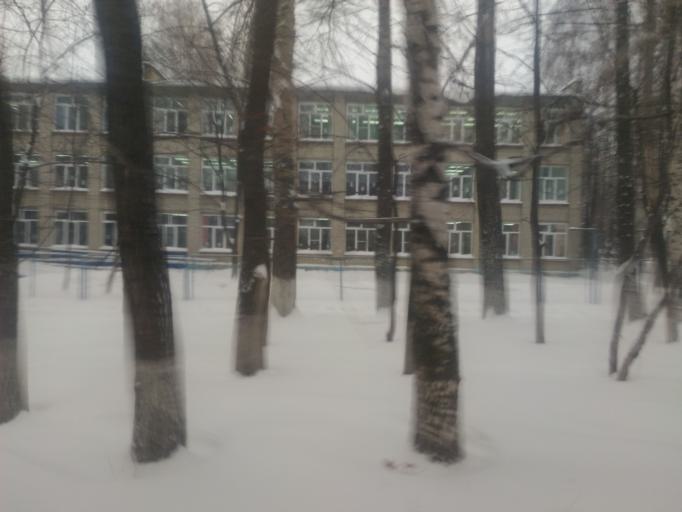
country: RU
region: Ulyanovsk
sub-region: Ulyanovskiy Rayon
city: Ulyanovsk
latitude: 54.3553
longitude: 48.3776
